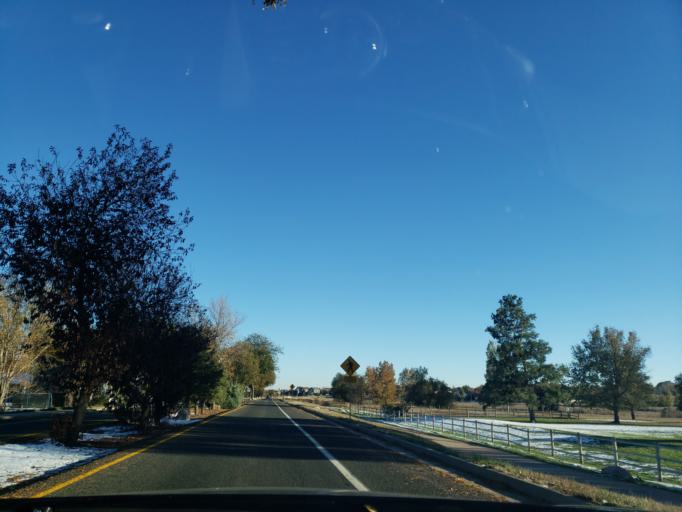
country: US
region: Colorado
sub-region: Larimer County
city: Fort Collins
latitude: 40.5126
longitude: -105.0718
